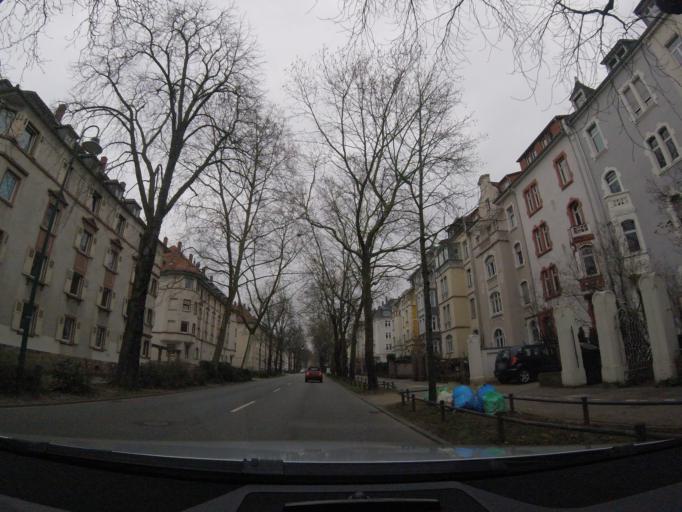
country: DE
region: Hesse
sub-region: Regierungsbezirk Darmstadt
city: Darmstadt
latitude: 49.8827
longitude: 8.6614
